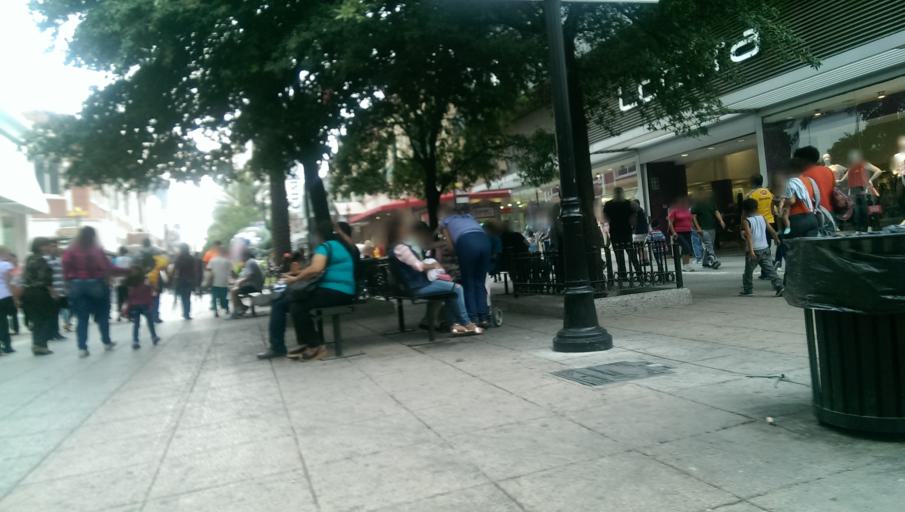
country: MX
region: Nuevo Leon
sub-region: Monterrey
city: Monterrey
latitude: 25.6674
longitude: -100.3123
